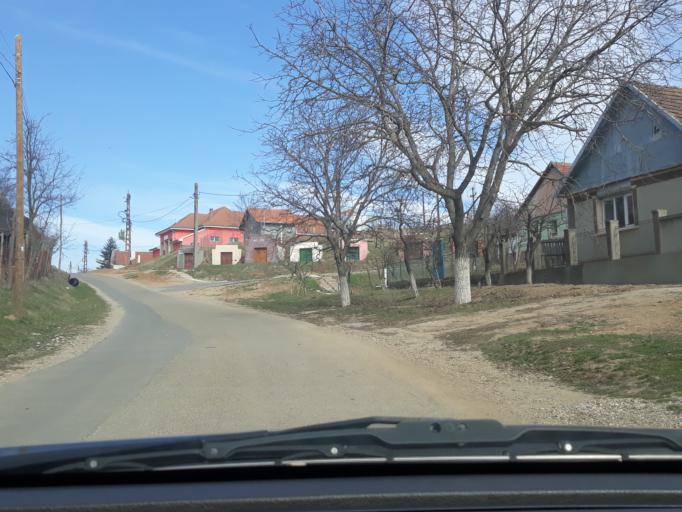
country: RO
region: Bihor
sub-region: Comuna Paleu
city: Paleu
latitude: 47.1134
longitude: 21.9577
